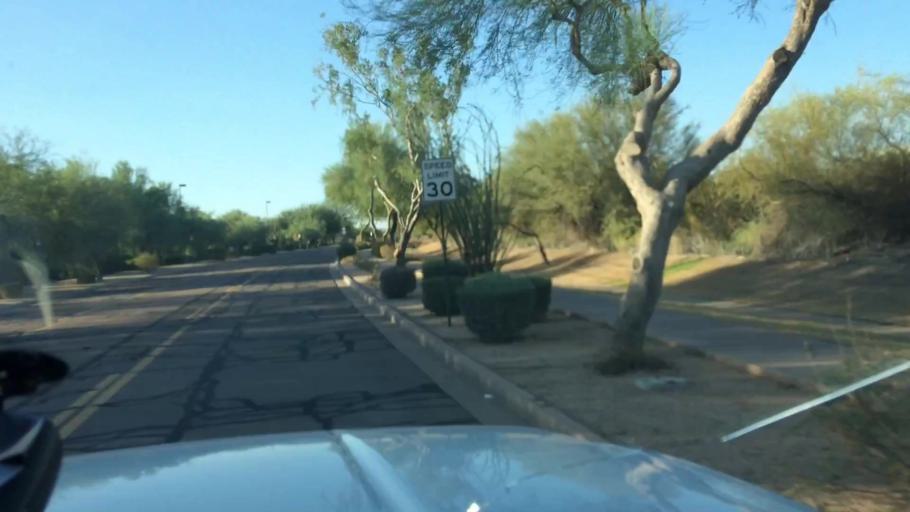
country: US
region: Arizona
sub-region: Maricopa County
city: Paradise Valley
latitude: 33.6467
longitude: -111.9029
